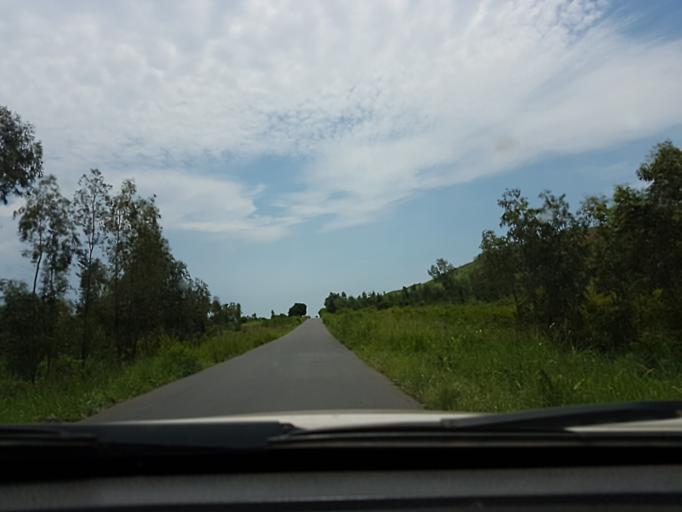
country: CD
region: South Kivu
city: Uvira
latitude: -3.2553
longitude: 29.1612
